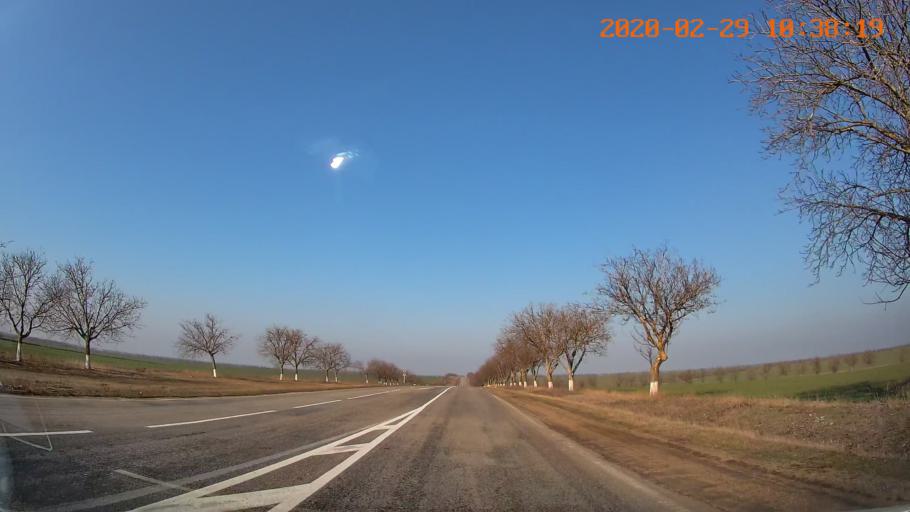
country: MD
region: Anenii Noi
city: Varnita
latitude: 47.0152
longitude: 29.4753
